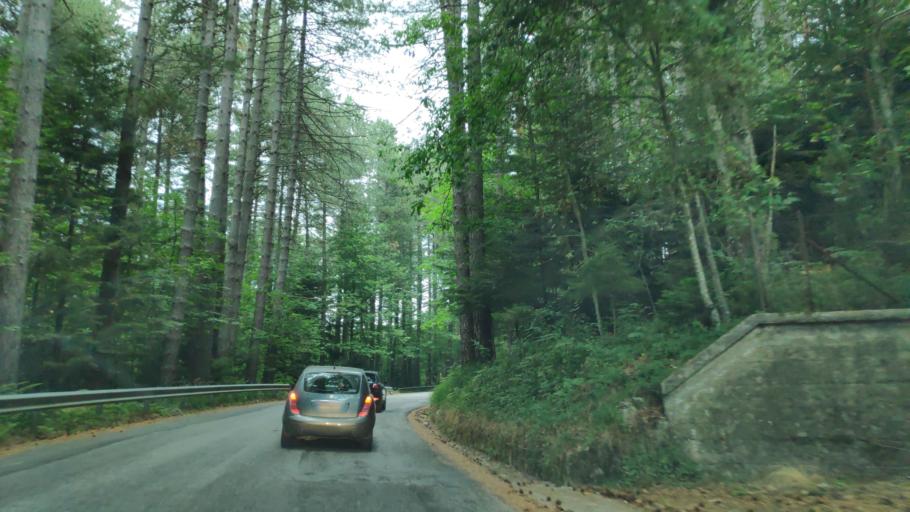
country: IT
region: Calabria
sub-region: Provincia di Vibo-Valentia
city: Mongiana
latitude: 38.5195
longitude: 16.3187
